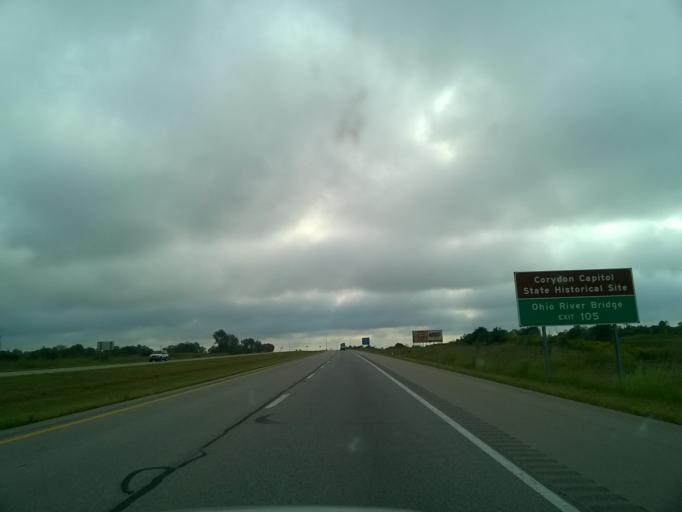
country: US
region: Indiana
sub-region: Harrison County
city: Corydon
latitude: 38.2390
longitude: -86.1396
